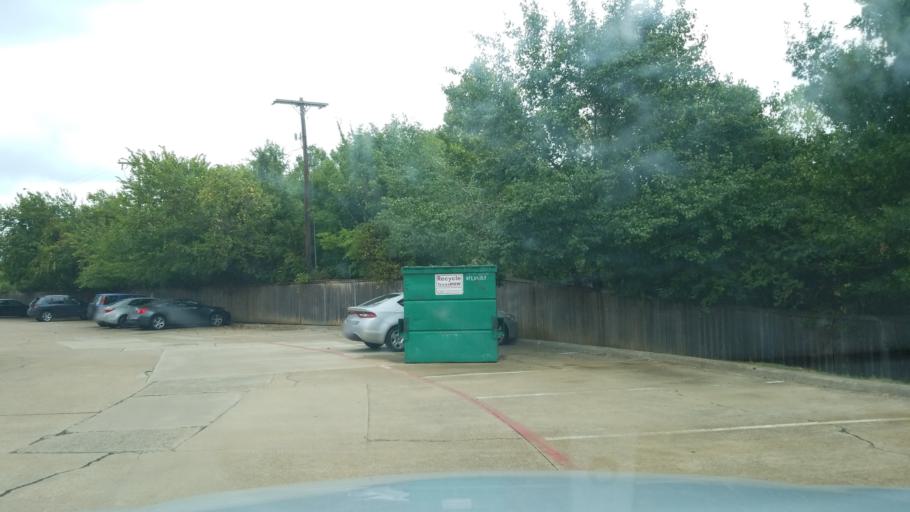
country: US
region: Texas
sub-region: Tarrant County
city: Euless
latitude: 32.8348
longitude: -97.1119
